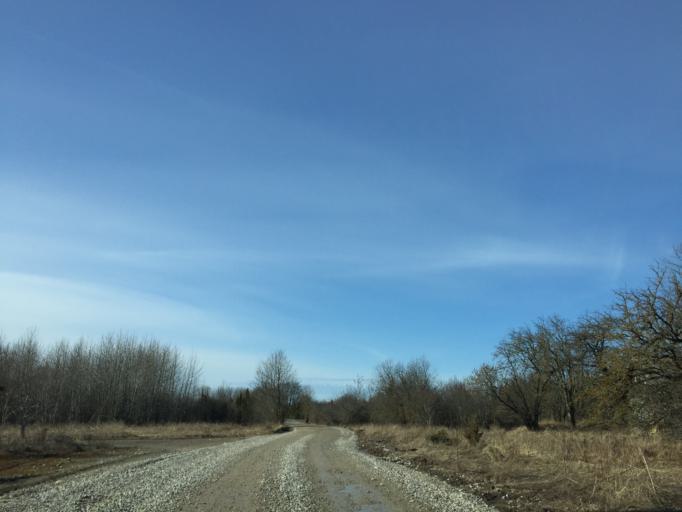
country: EE
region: Laeaene
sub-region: Haapsalu linn
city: Haapsalu
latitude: 58.6654
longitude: 23.5229
